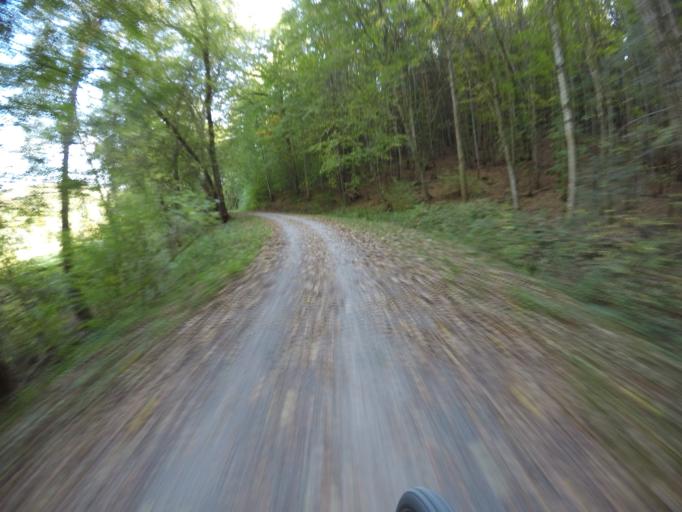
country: DE
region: Baden-Wuerttemberg
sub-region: Regierungsbezirk Stuttgart
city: Filderstadt
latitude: 48.6315
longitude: 9.1867
